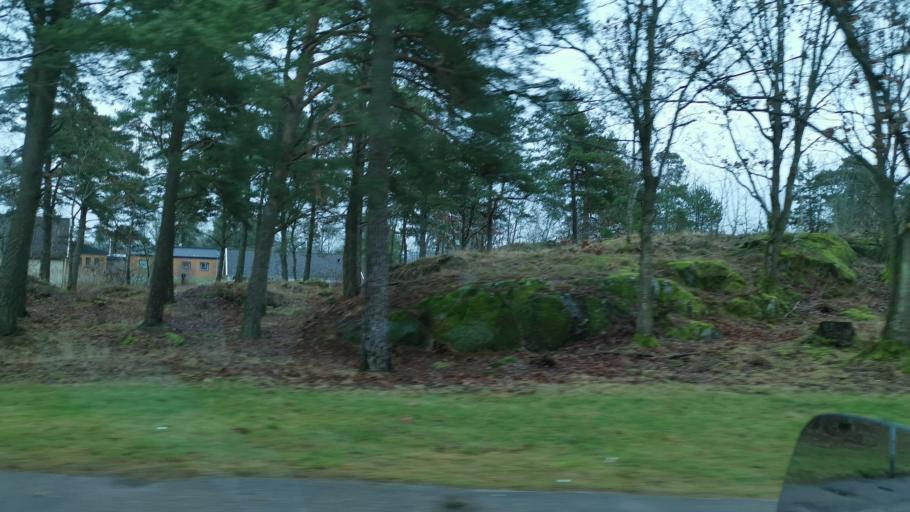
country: SE
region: Vaestra Goetaland
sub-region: Vanersborgs Kommun
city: Vanersborg
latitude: 58.3630
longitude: 12.3483
